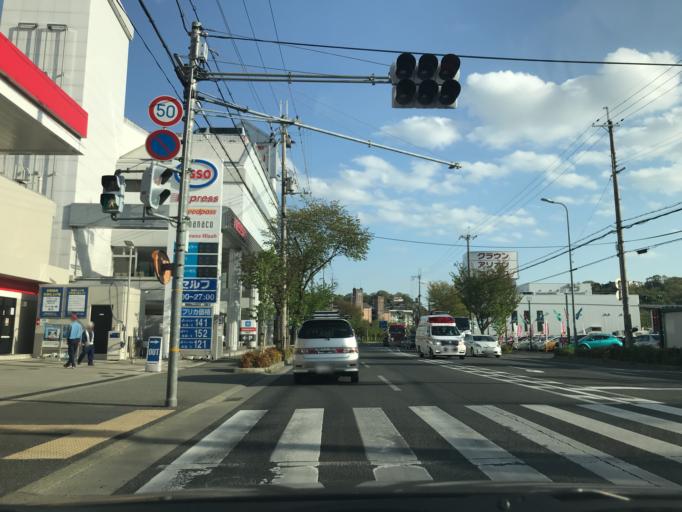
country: JP
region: Osaka
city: Ikeda
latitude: 34.8593
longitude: 135.4162
